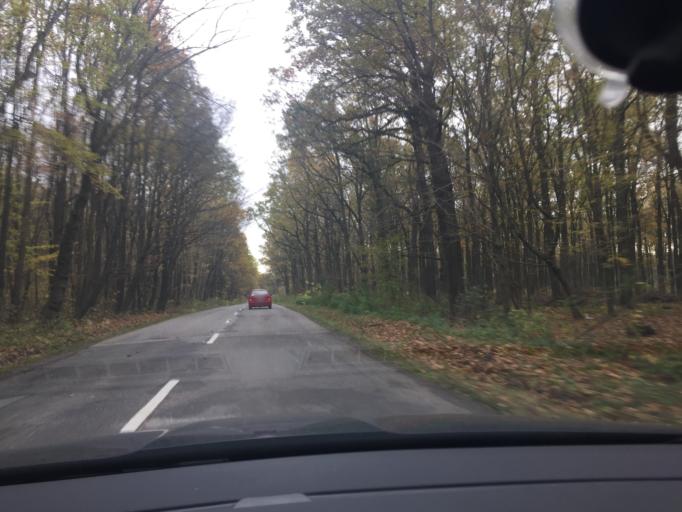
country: SK
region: Presovsky
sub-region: Okres Presov
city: Presov
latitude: 48.9380
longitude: 21.3107
